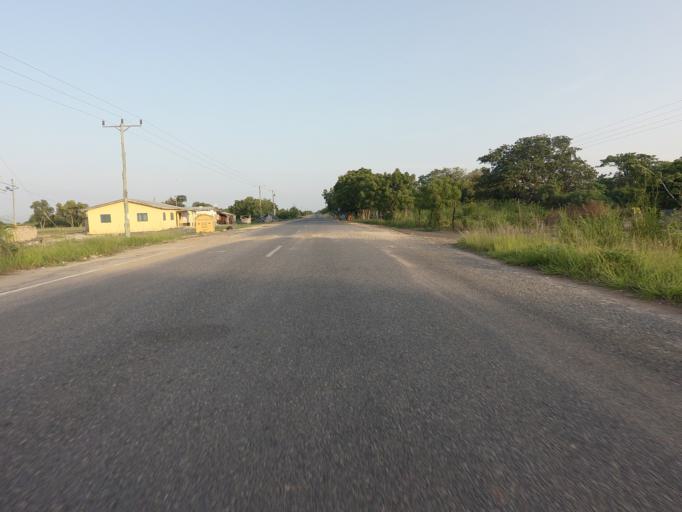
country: GH
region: Volta
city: Anloga
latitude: 5.9082
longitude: 0.7103
